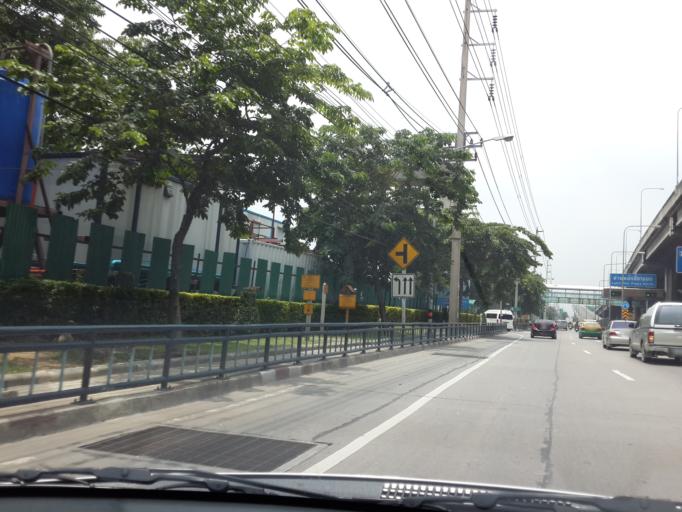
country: TH
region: Bangkok
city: Lak Si
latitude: 13.8866
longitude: 100.5826
